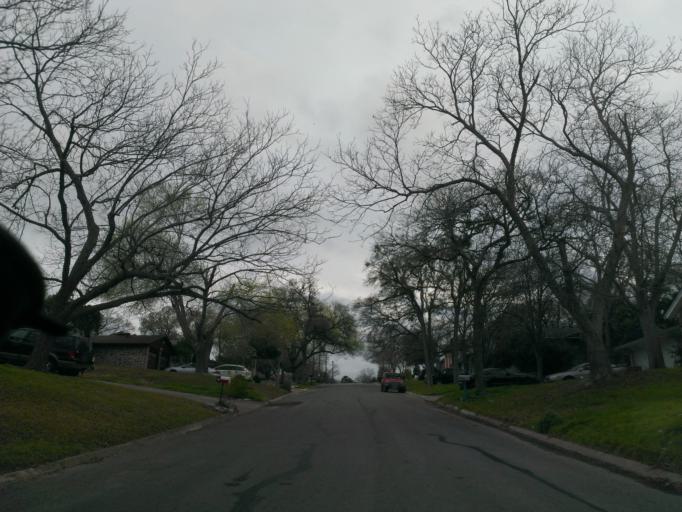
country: US
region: Texas
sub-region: Travis County
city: Wells Branch
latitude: 30.3884
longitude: -97.6796
